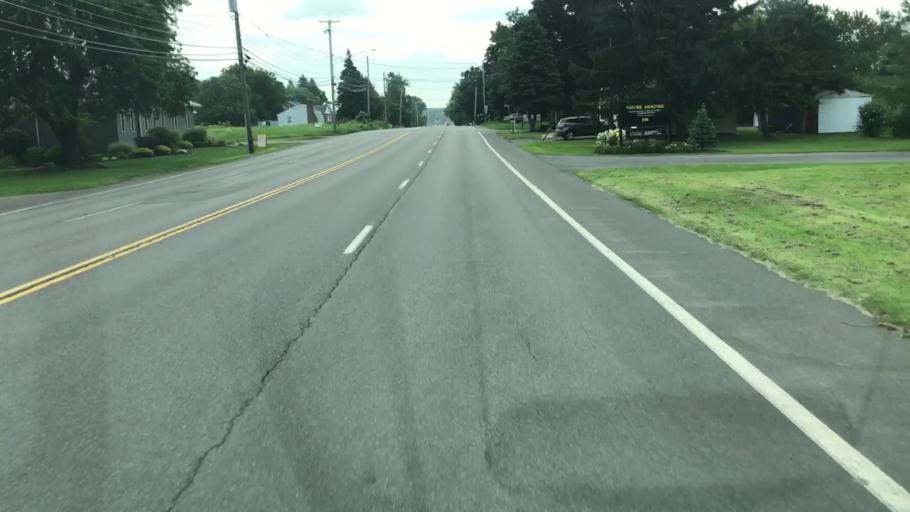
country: US
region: New York
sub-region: Onondaga County
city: Galeville
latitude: 43.0974
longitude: -76.1788
